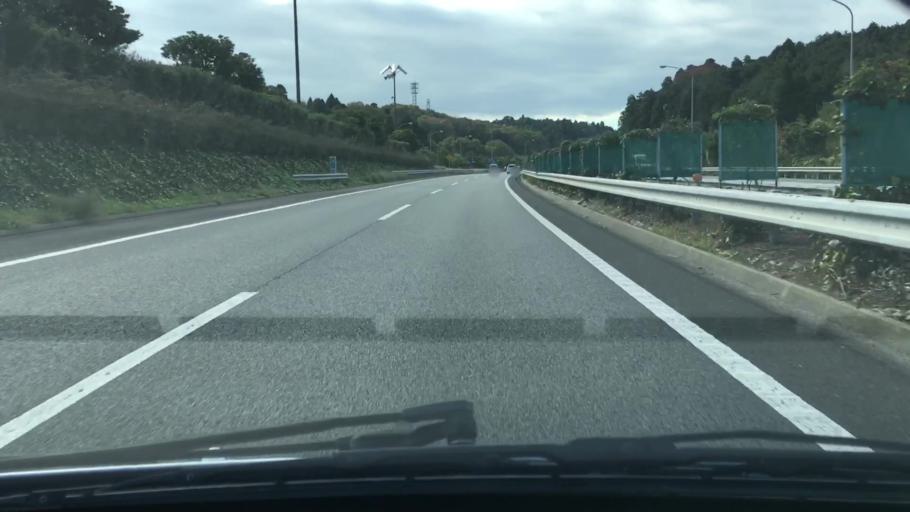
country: JP
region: Chiba
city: Ichihara
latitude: 35.4593
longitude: 140.0853
